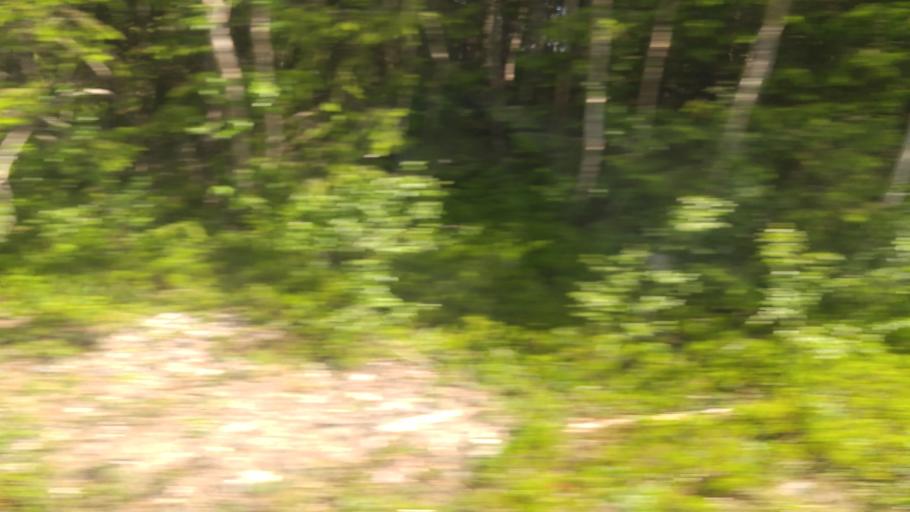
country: NO
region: Nord-Trondelag
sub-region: Meraker
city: Meraker
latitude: 63.3127
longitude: 12.2390
